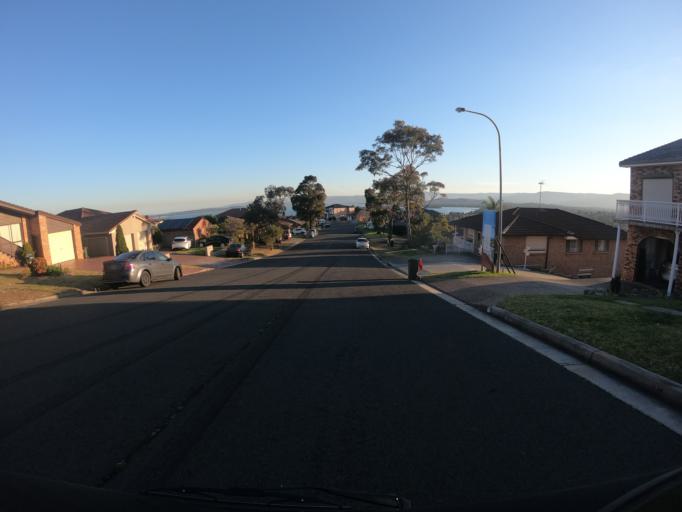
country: AU
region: New South Wales
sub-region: Wollongong
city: Berkeley
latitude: -34.4767
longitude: 150.8593
